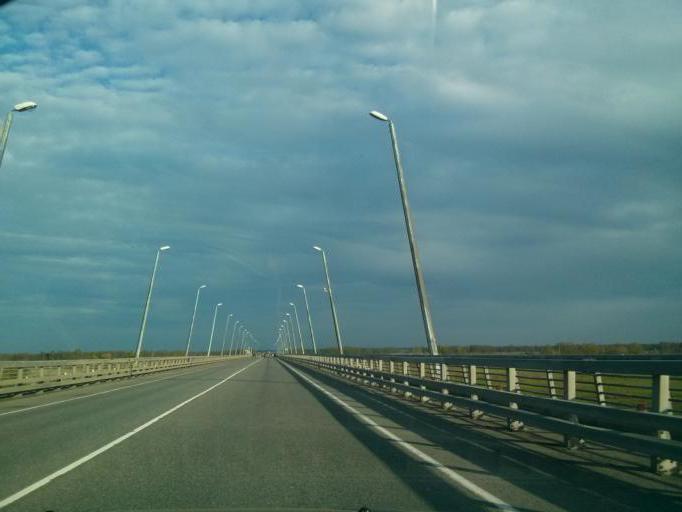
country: RU
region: Vladimir
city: Murom
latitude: 55.6134
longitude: 42.0770
